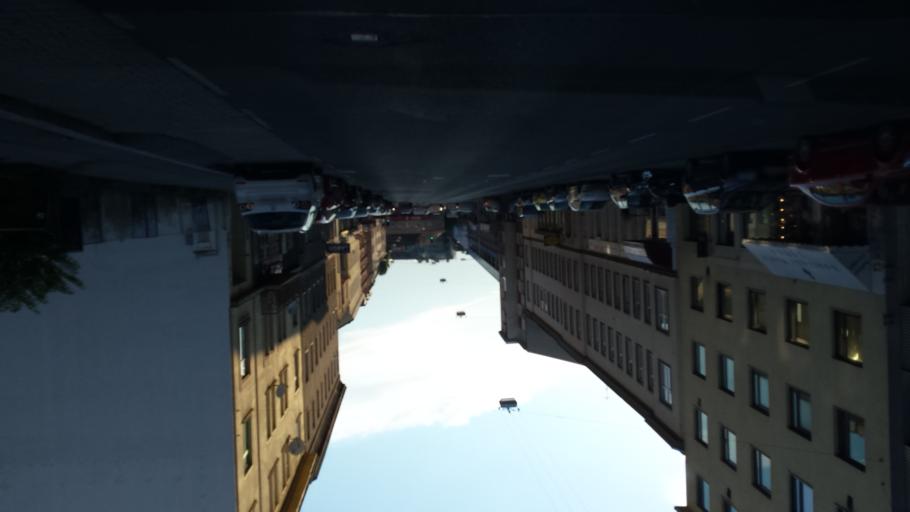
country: AT
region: Vienna
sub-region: Wien Stadt
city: Vienna
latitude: 48.2589
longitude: 16.4020
